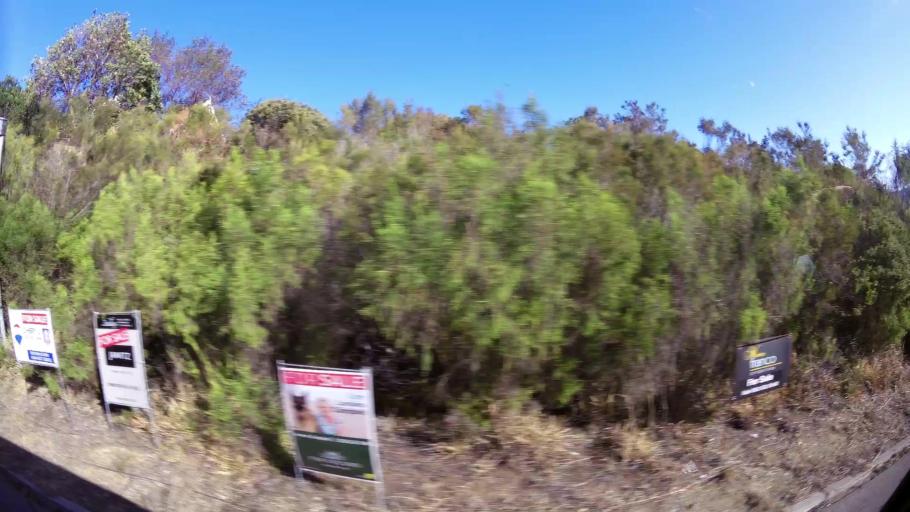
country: ZA
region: Western Cape
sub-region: Eden District Municipality
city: George
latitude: -33.9898
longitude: 22.5801
